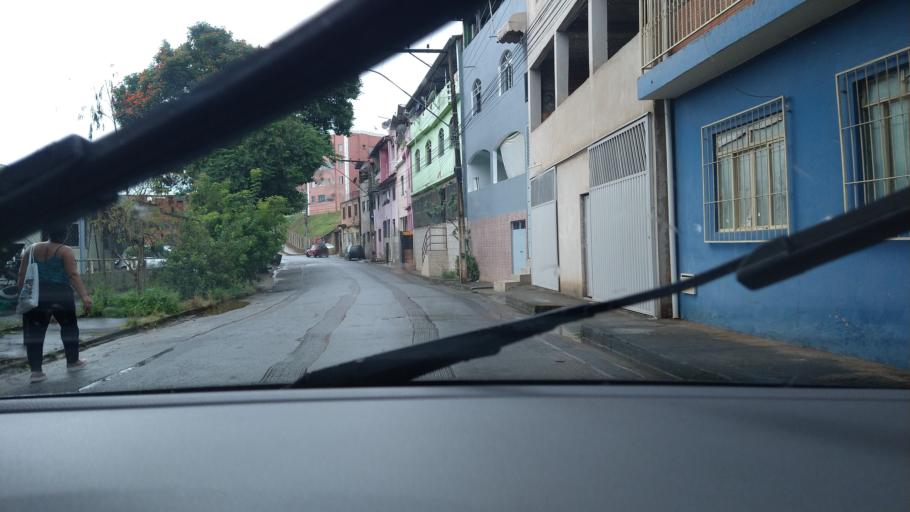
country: BR
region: Minas Gerais
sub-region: Ponte Nova
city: Ponte Nova
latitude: -20.3994
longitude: -42.9007
